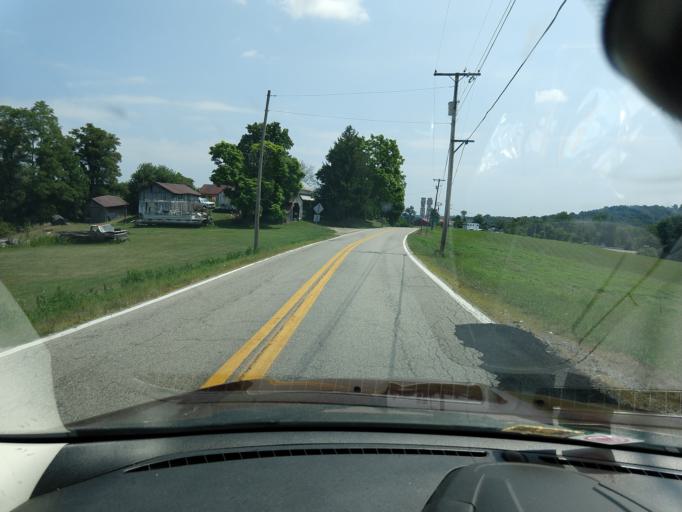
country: US
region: West Virginia
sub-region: Mason County
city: New Haven
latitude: 38.8641
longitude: -81.8863
